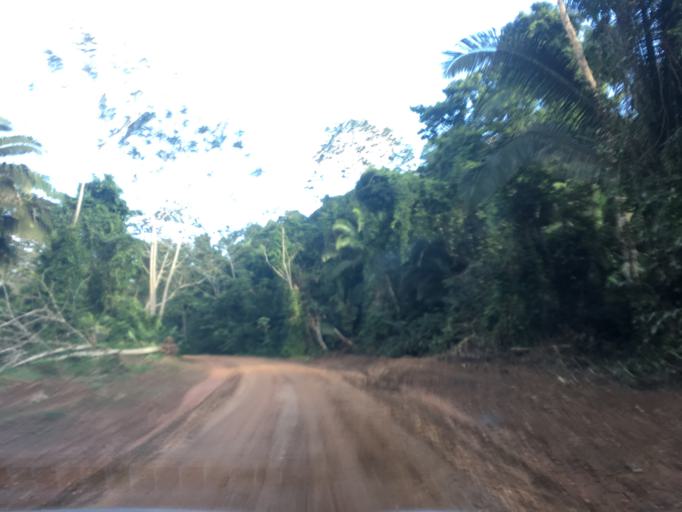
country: BZ
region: Stann Creek
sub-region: Dangriga
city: Dangriga
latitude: 16.7996
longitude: -88.4036
